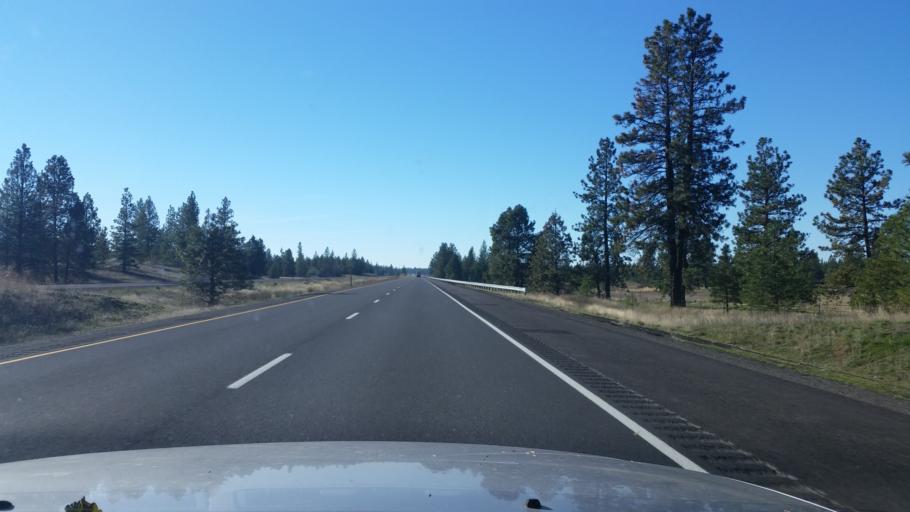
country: US
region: Washington
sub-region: Spokane County
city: Medical Lake
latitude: 47.4545
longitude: -117.7645
